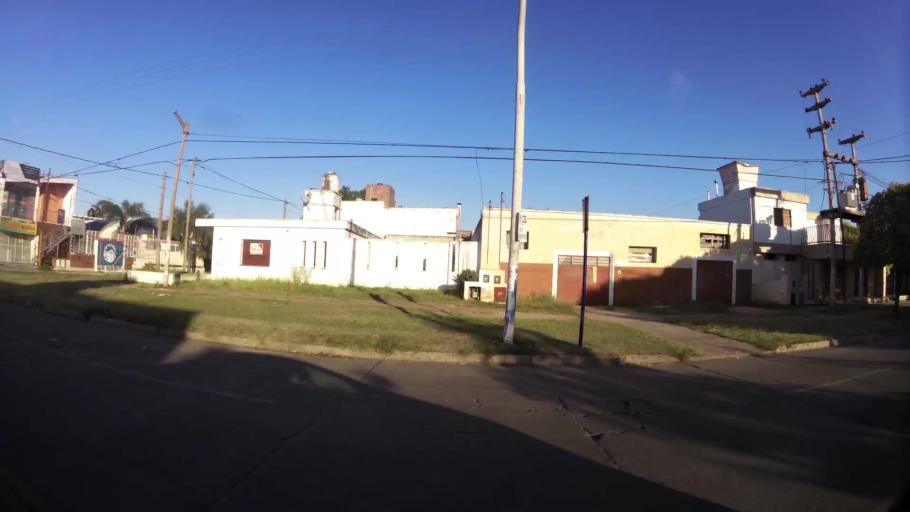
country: AR
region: Cordoba
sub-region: Departamento de Capital
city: Cordoba
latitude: -31.3756
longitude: -64.2140
